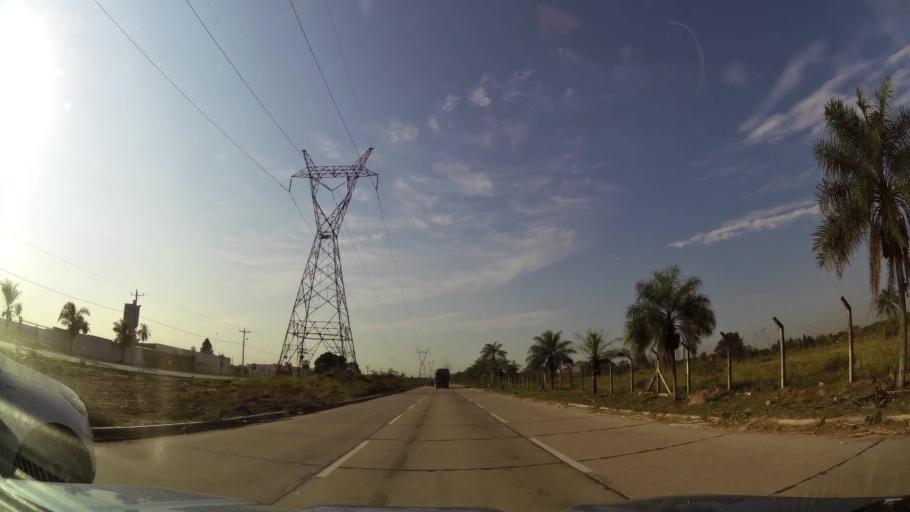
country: BO
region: Santa Cruz
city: Santa Cruz de la Sierra
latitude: -17.6986
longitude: -63.1345
